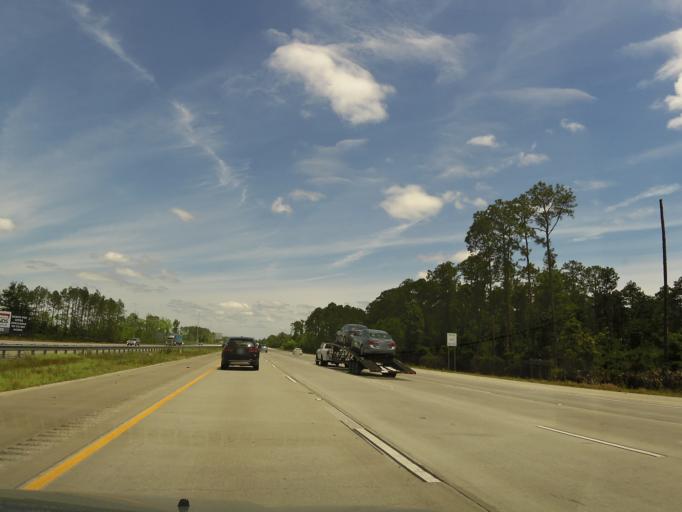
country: US
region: Georgia
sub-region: Glynn County
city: Country Club Estates
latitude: 31.2646
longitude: -81.4937
